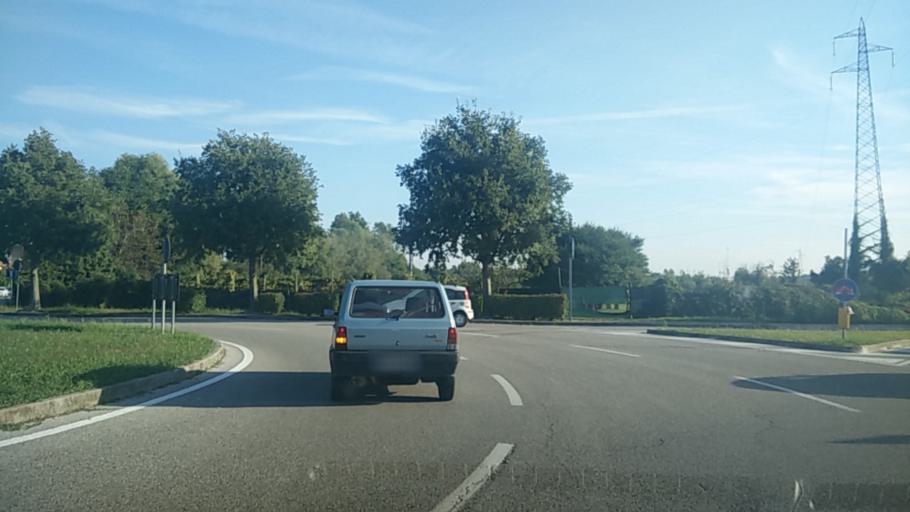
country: IT
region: Veneto
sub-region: Provincia di Venezia
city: Zelarino
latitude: 45.5172
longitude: 12.2072
